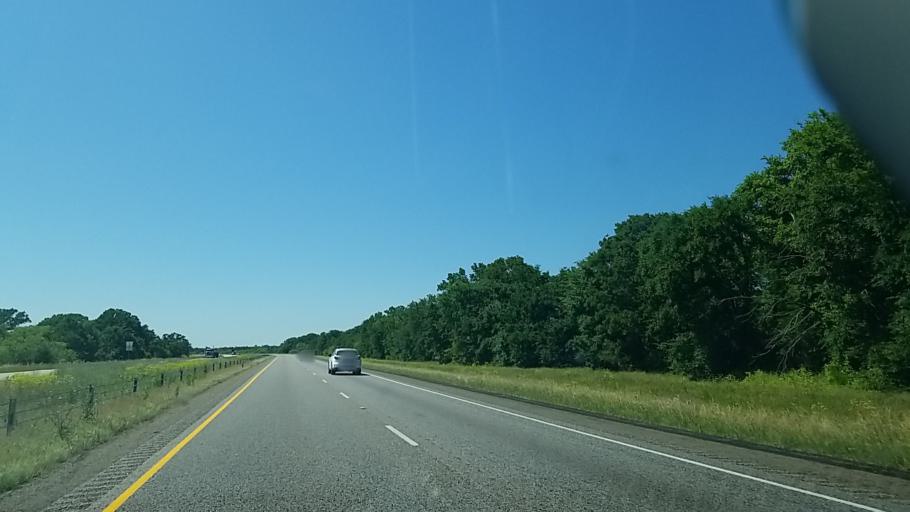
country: US
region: Texas
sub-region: Freestone County
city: Wortham
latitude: 31.8564
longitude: -96.3064
